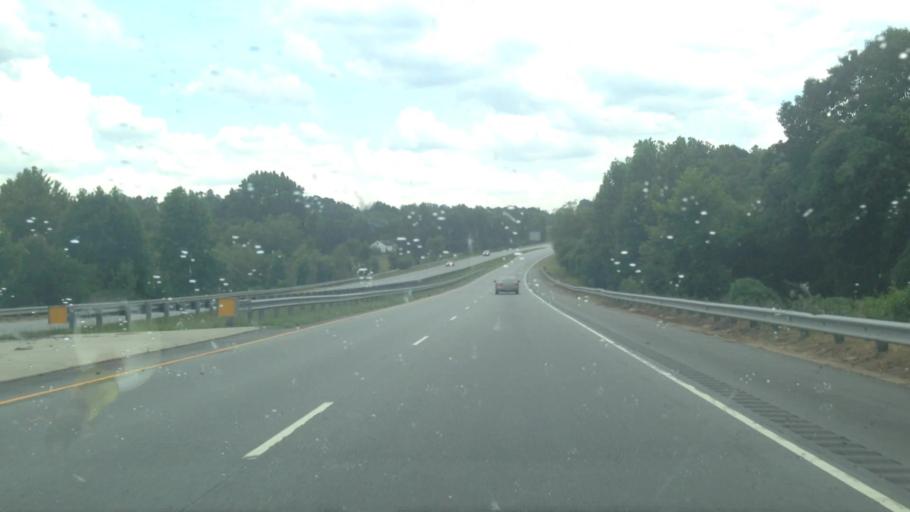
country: US
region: North Carolina
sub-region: Rockingham County
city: Madison
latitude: 36.3645
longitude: -79.9447
